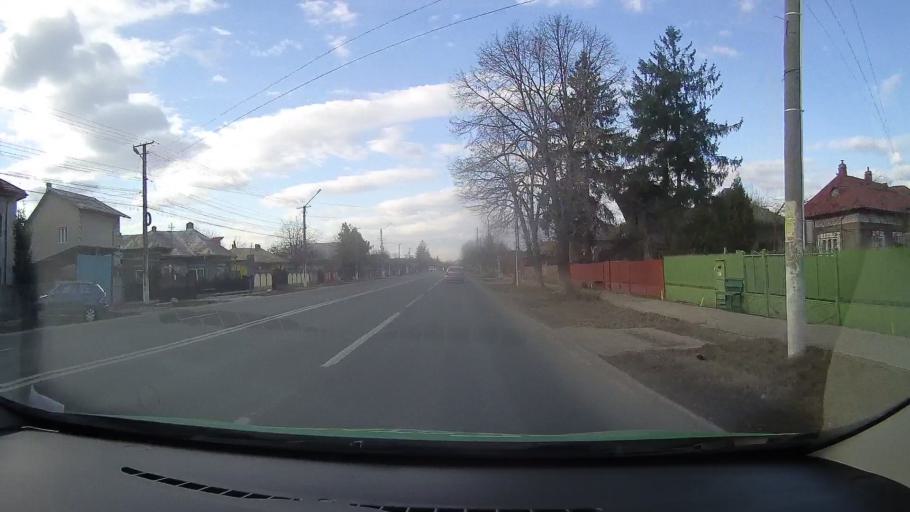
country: RO
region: Dambovita
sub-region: Comuna Ulmi
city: Ulmi
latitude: 44.8972
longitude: 25.4998
